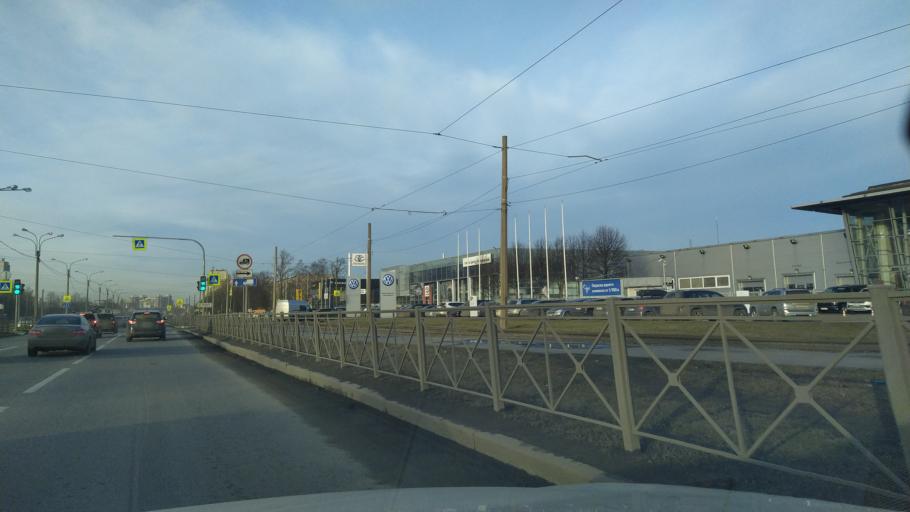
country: RU
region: Leningrad
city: Akademicheskoe
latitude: 60.0066
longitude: 30.4356
